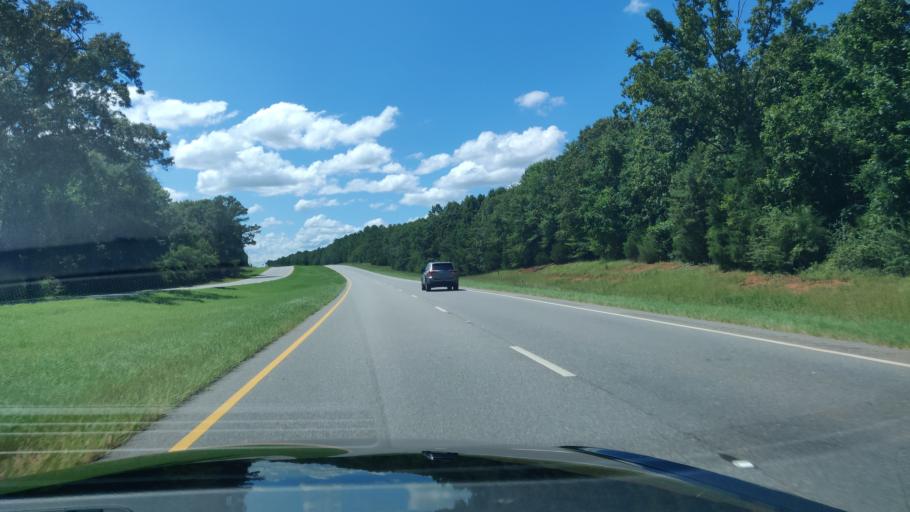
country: US
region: Georgia
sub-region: Webster County
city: Preston
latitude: 31.9105
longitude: -84.5309
